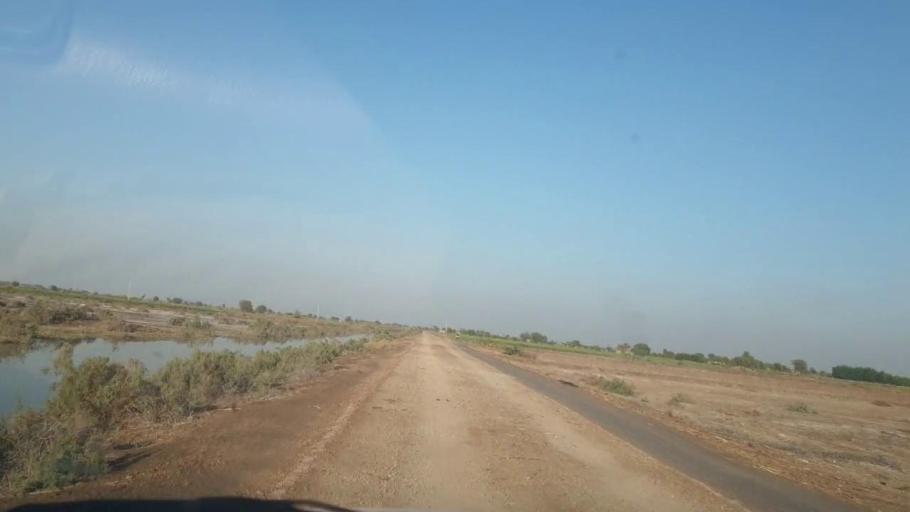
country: PK
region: Sindh
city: Mirpur Khas
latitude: 25.4492
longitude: 69.1087
